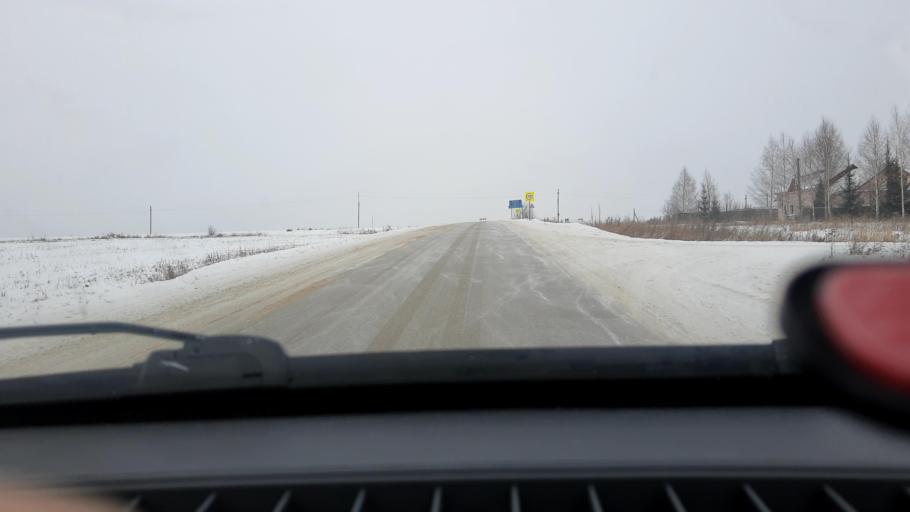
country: RU
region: Bashkortostan
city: Iglino
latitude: 54.7070
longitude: 56.4024
